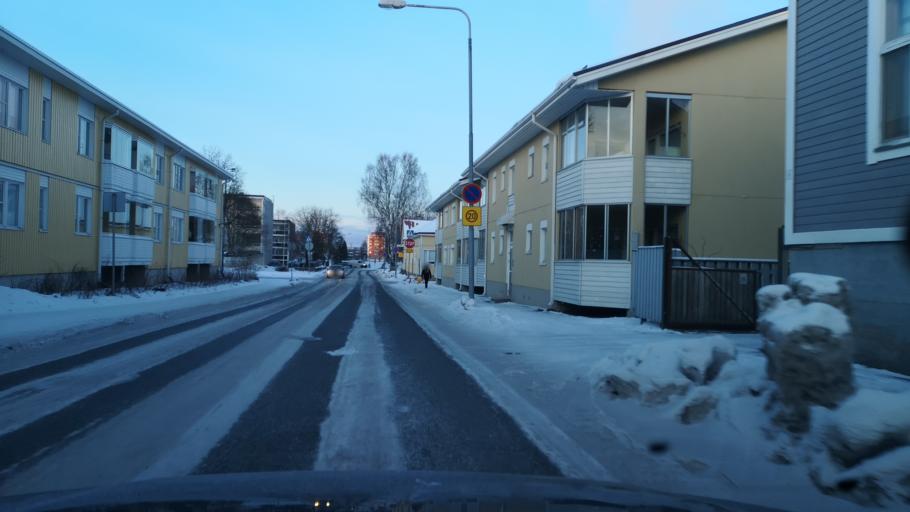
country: FI
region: Satakunta
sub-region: Pori
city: Pori
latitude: 61.4836
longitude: 21.8074
